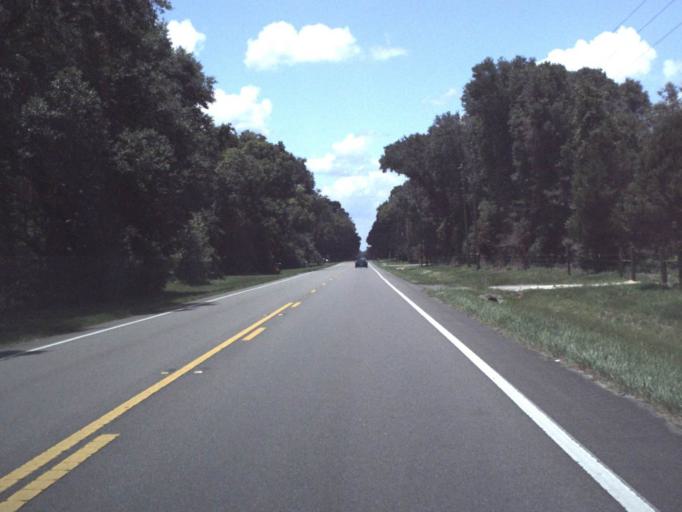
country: US
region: Florida
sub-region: Levy County
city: Williston
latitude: 29.4480
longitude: -82.4698
